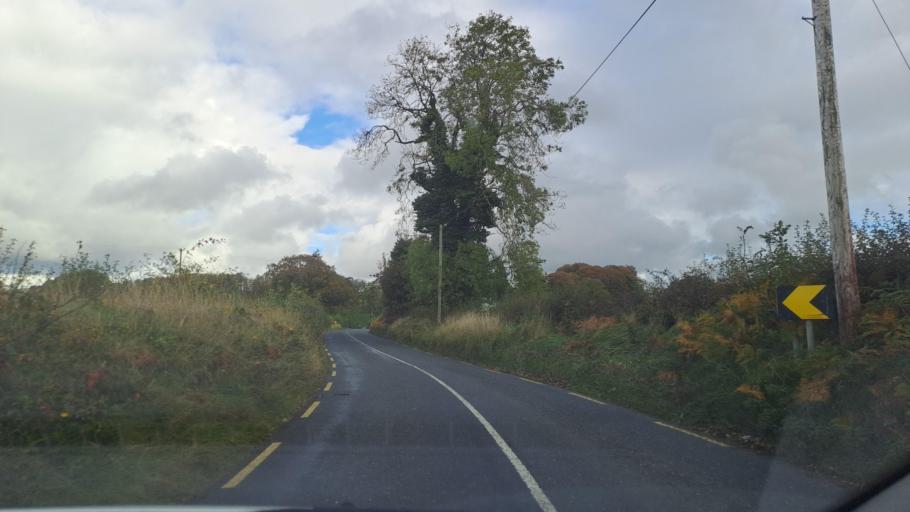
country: IE
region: Ulster
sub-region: An Cabhan
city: Virginia
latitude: 53.8297
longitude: -7.0548
